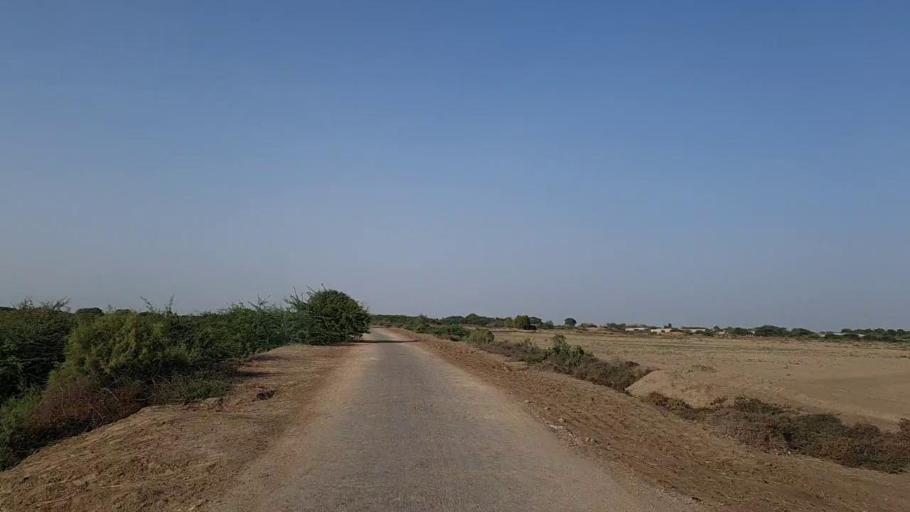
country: PK
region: Sindh
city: Jati
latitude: 24.3096
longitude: 68.1674
